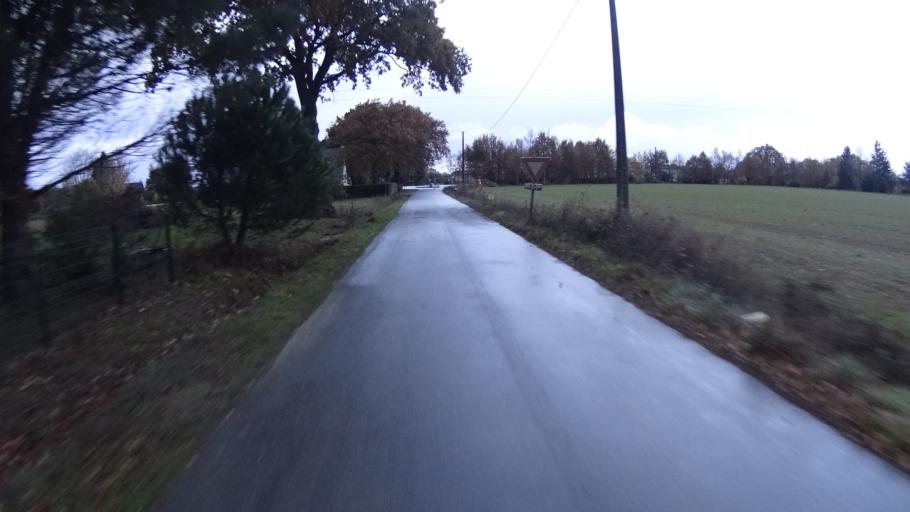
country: FR
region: Brittany
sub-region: Departement d'Ille-et-Vilaine
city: Bains-sur-Oust
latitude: 47.6872
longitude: -2.0514
